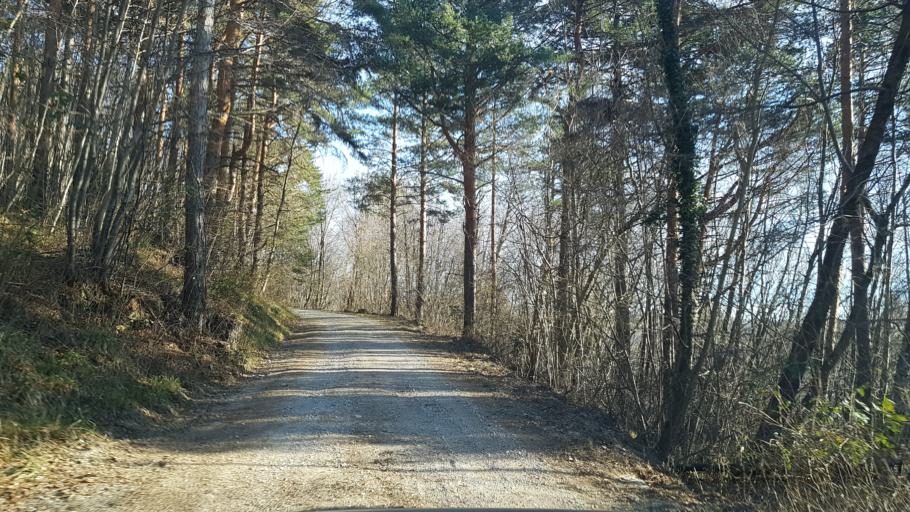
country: SI
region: Nova Gorica
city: Kromberk
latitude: 46.0130
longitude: 13.7021
